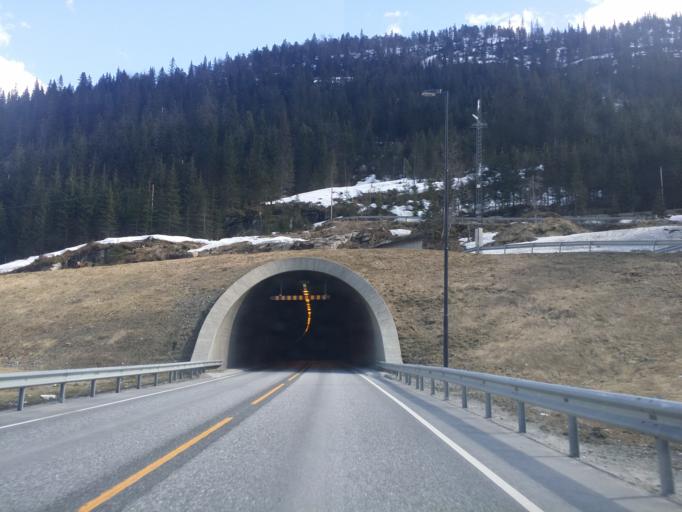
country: NO
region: Hordaland
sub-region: Granvin
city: Granvin
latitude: 60.5850
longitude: 6.6135
